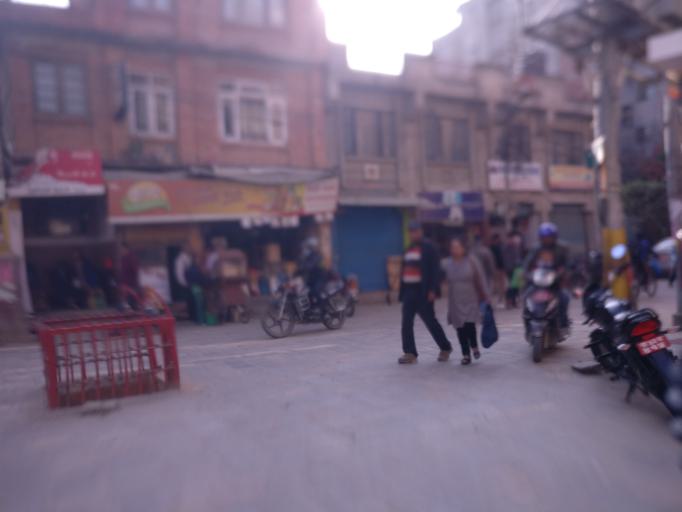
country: NP
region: Central Region
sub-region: Bagmati Zone
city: Kathmandu
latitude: 27.7006
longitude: 85.3076
